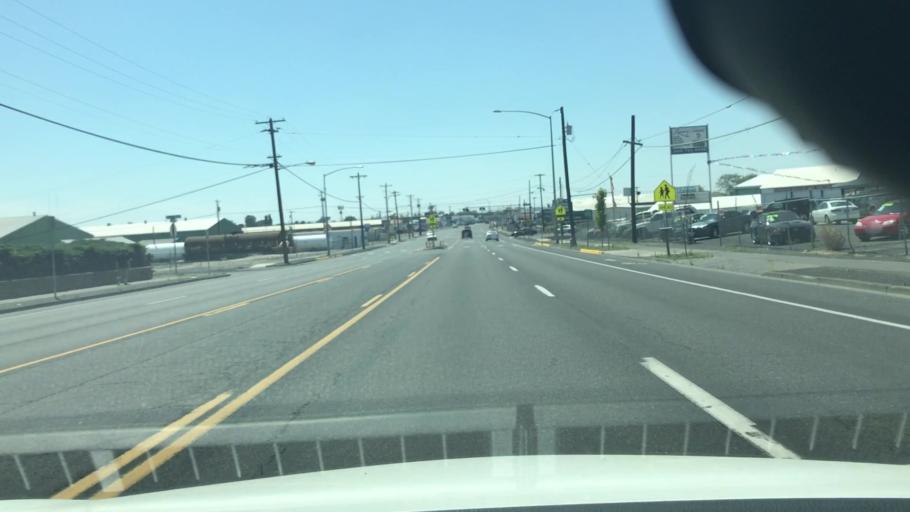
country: US
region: Washington
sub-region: Grant County
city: Moses Lake
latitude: 47.1195
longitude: -119.2940
